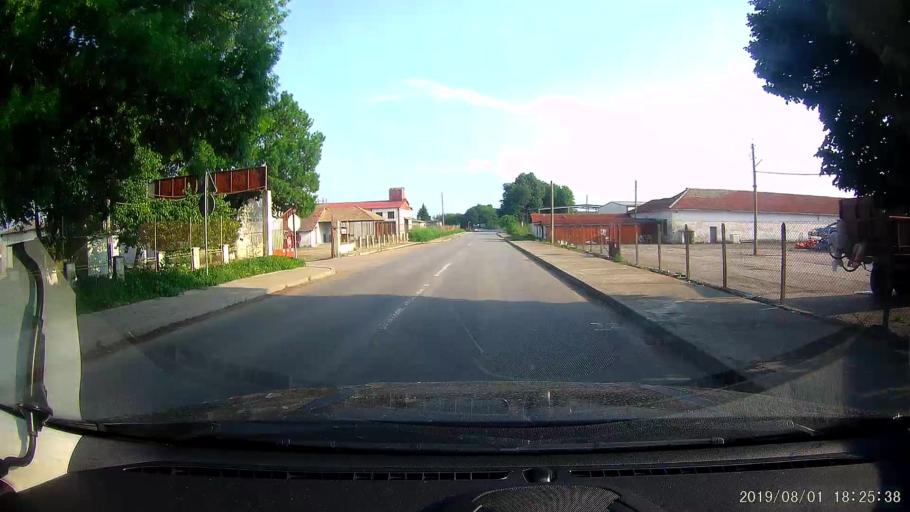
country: BG
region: Shumen
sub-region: Obshtina Venets
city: Venets
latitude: 43.6146
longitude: 26.9955
